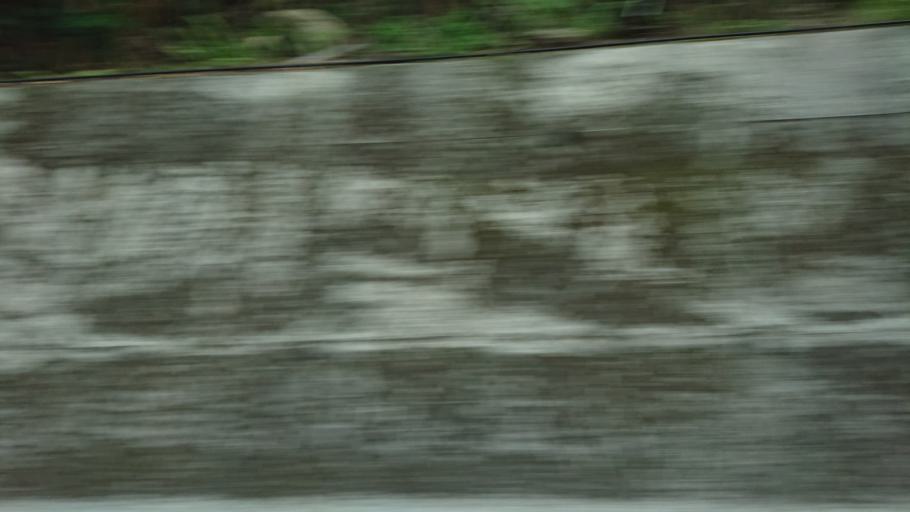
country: TW
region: Taiwan
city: Daxi
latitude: 24.8665
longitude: 121.4206
